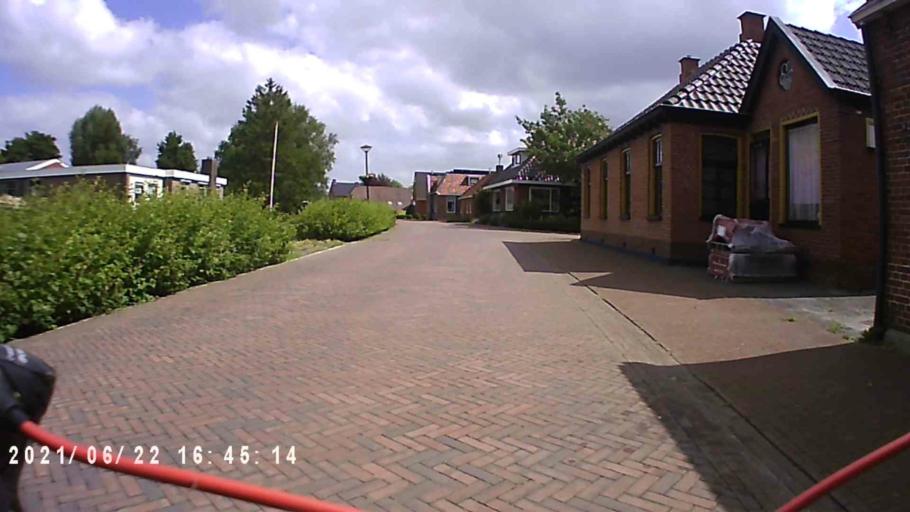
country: NL
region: Groningen
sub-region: Gemeente Bedum
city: Bedum
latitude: 53.3463
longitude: 6.6390
